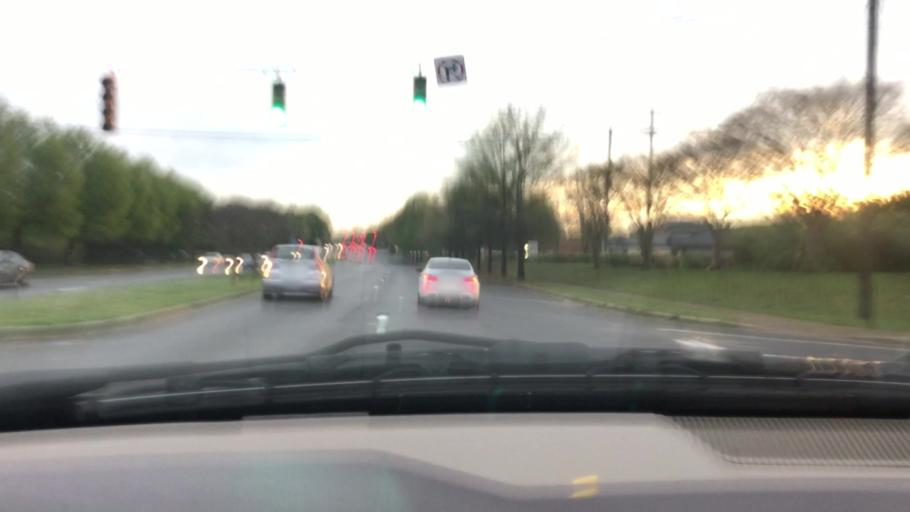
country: US
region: North Carolina
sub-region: Mecklenburg County
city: Huntersville
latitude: 35.4087
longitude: -80.8591
